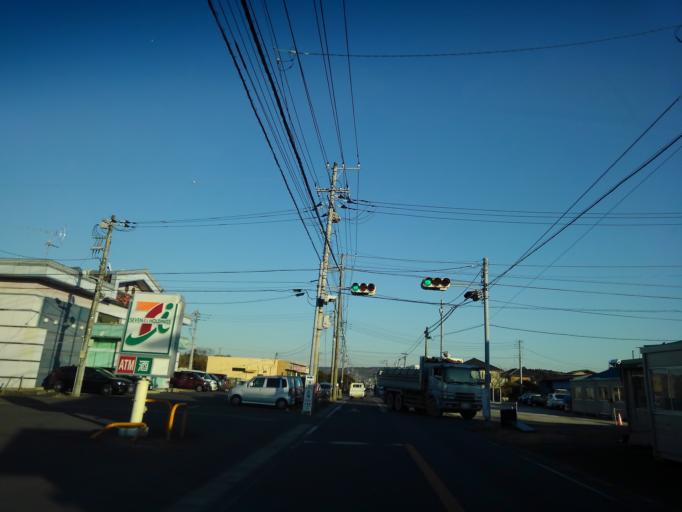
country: JP
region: Chiba
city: Kimitsu
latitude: 35.3071
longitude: 139.9472
